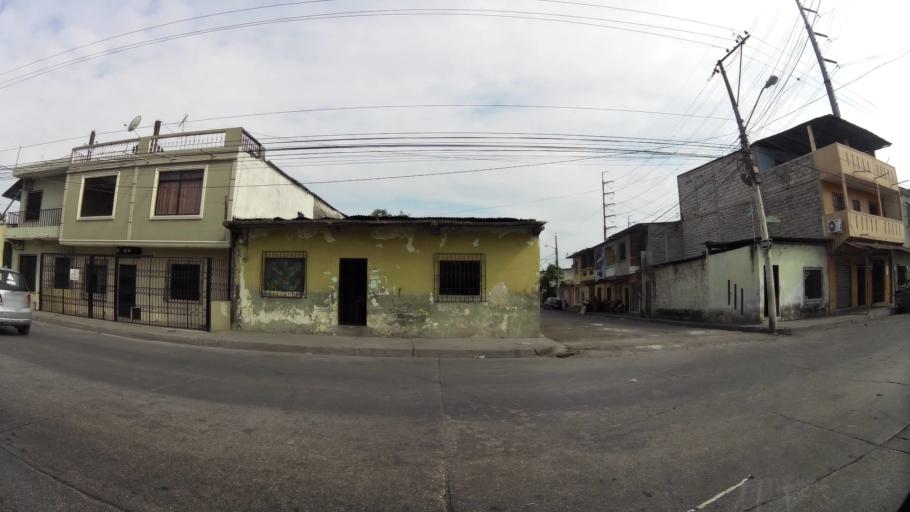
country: EC
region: Guayas
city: Guayaquil
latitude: -2.2544
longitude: -79.9060
